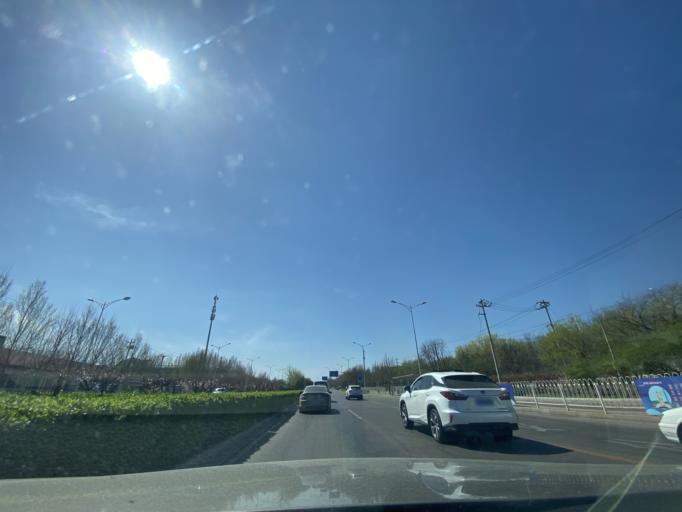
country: CN
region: Beijing
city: Sijiqing
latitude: 39.9419
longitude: 116.2405
